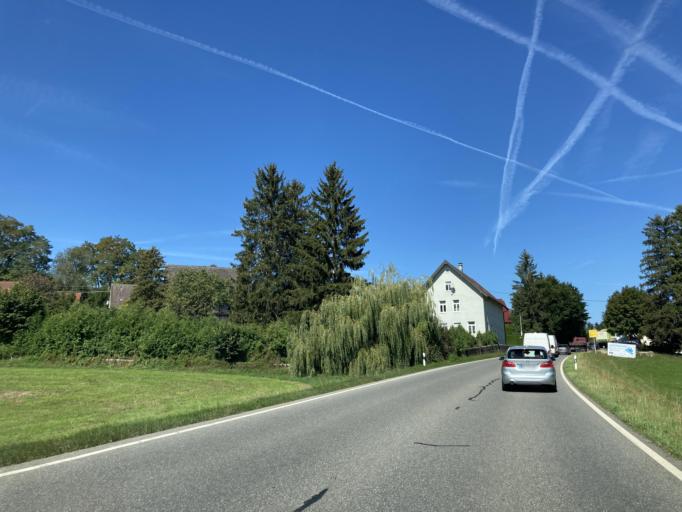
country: DE
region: Baden-Wuerttemberg
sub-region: Tuebingen Region
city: Unlingen
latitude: 48.1522
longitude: 9.5279
